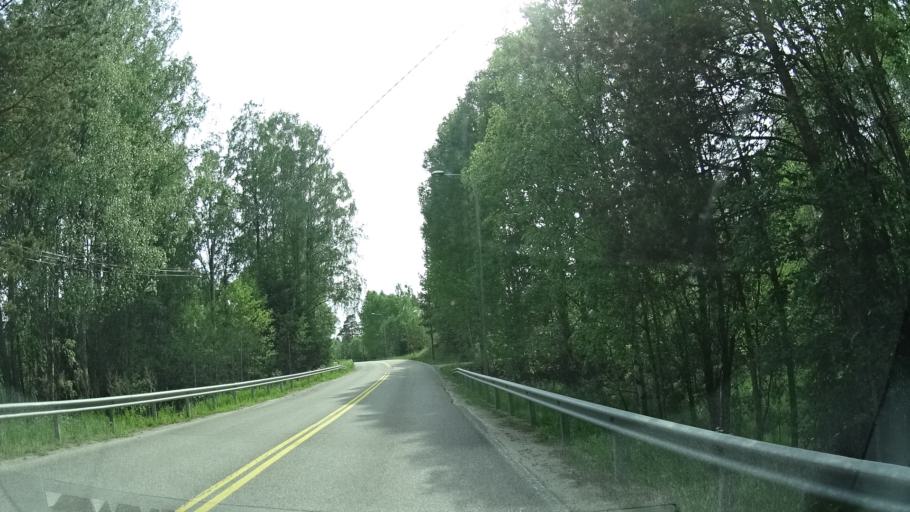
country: FI
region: Uusimaa
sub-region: Helsinki
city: Kirkkonummi
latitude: 60.0473
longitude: 24.5024
